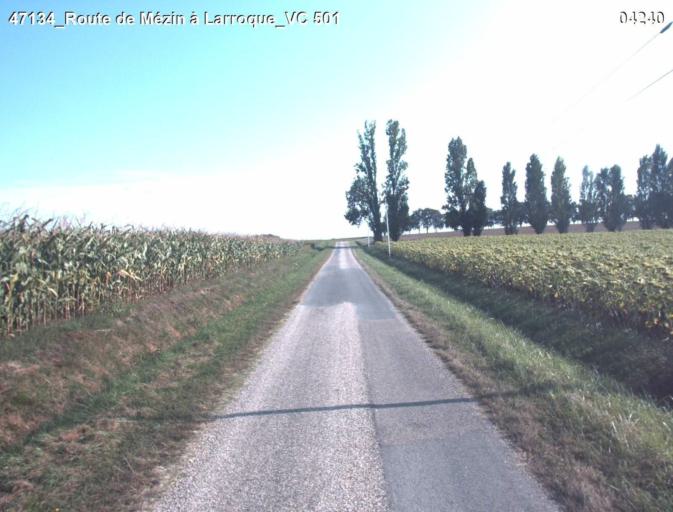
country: FR
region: Aquitaine
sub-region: Departement du Lot-et-Garonne
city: Mezin
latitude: 44.0324
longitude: 0.2676
